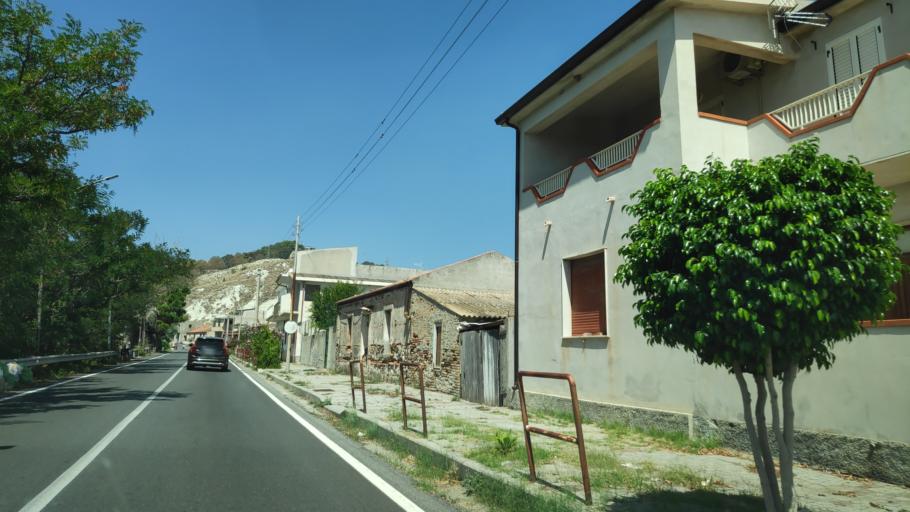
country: IT
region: Calabria
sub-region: Provincia di Reggio Calabria
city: Palizzi Marina
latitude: 37.9237
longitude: 16.0416
